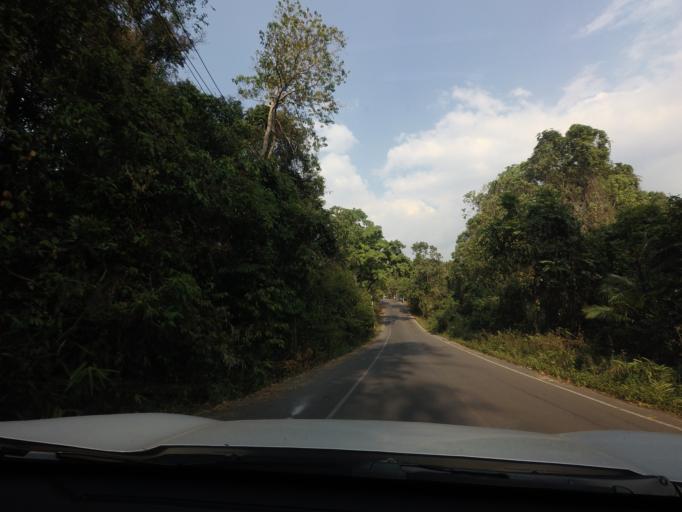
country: TH
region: Nakhon Ratchasima
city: Pak Chong
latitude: 14.4308
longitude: 101.3991
